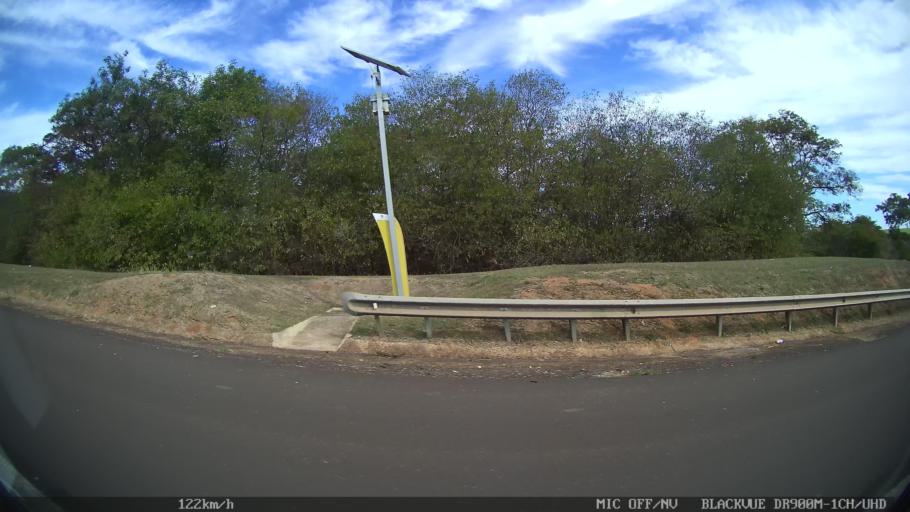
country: BR
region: Sao Paulo
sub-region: Matao
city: Matao
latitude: -21.5566
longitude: -48.4813
